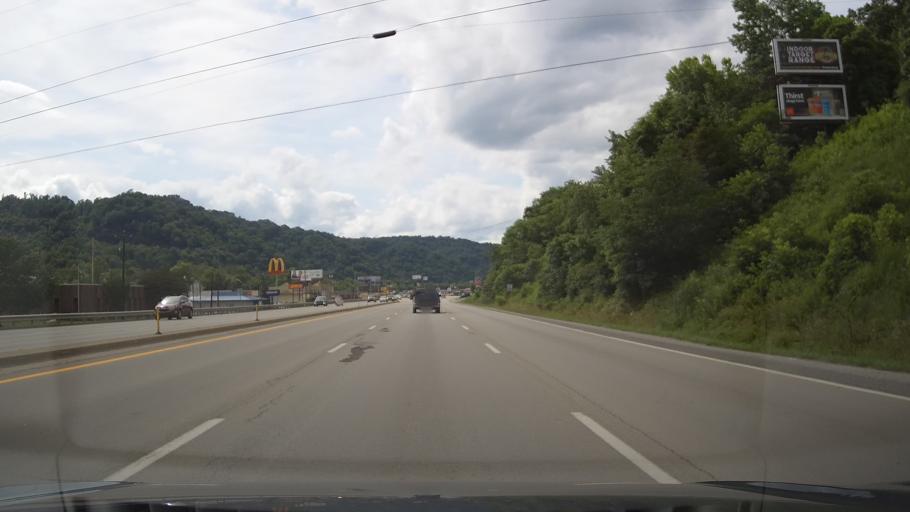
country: US
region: Kentucky
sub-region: Pike County
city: Coal Run Village
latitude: 37.5173
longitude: -82.5630
